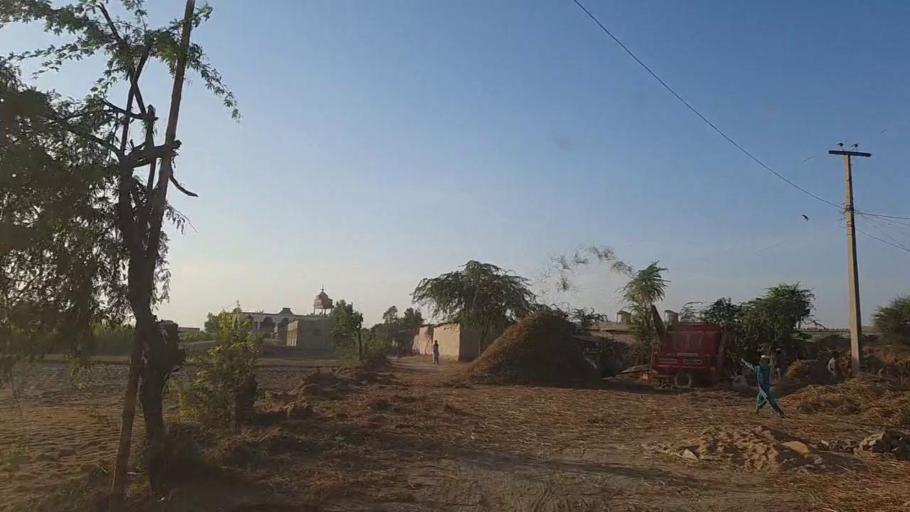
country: PK
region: Sindh
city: Mirpur Batoro
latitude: 24.6808
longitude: 68.2163
